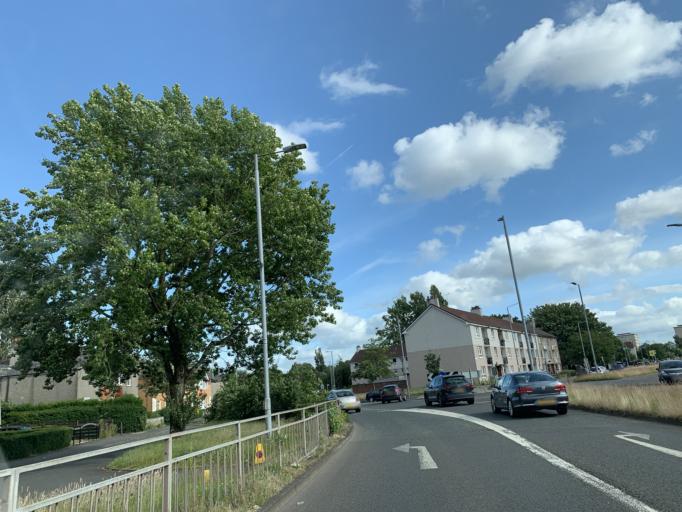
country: GB
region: Scotland
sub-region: Renfrewshire
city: Renfrew
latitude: 55.8519
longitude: -4.3629
